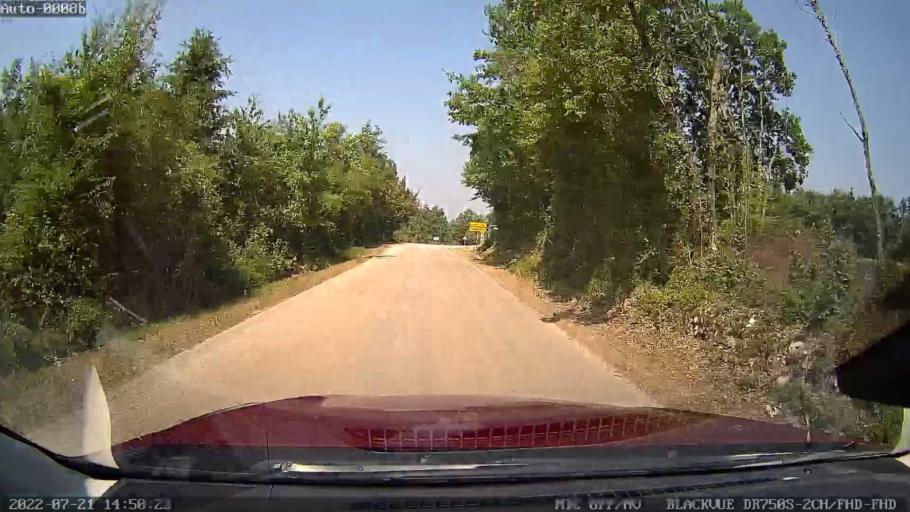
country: HR
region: Istarska
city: Pazin
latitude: 45.1600
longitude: 13.9152
